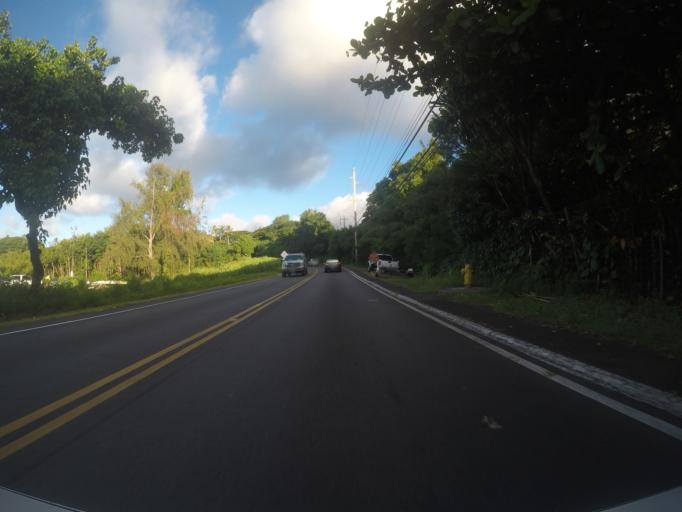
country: US
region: Hawaii
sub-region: Honolulu County
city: He'eia
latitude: 21.4423
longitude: -157.8114
